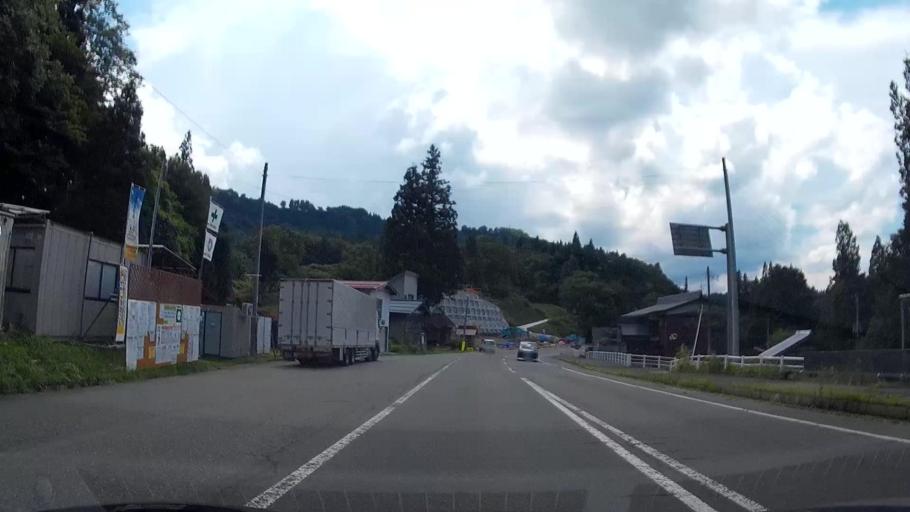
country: JP
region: Niigata
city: Tokamachi
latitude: 36.9954
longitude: 138.6158
